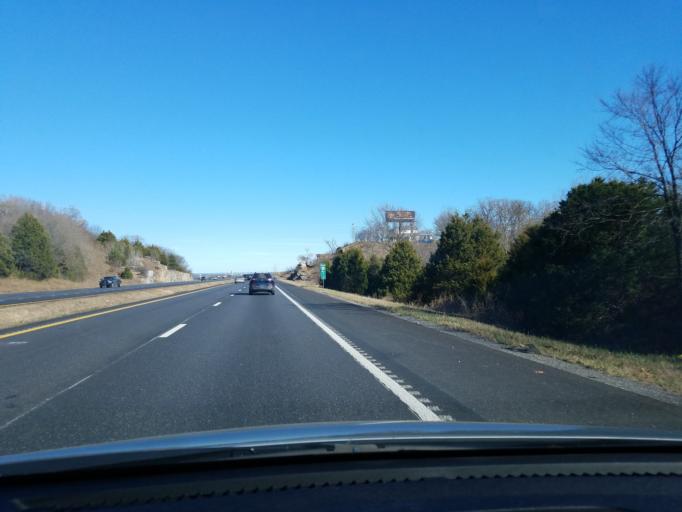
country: US
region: Missouri
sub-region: Taney County
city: Hollister
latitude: 36.5852
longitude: -93.2341
